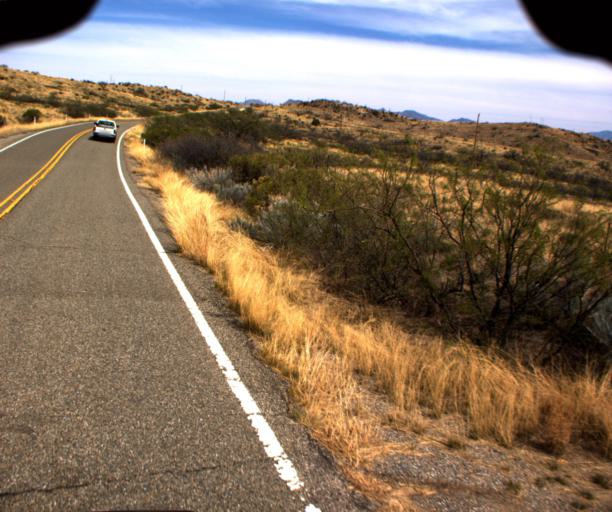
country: US
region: Arizona
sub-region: Cochise County
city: Willcox
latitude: 32.1673
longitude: -109.5857
